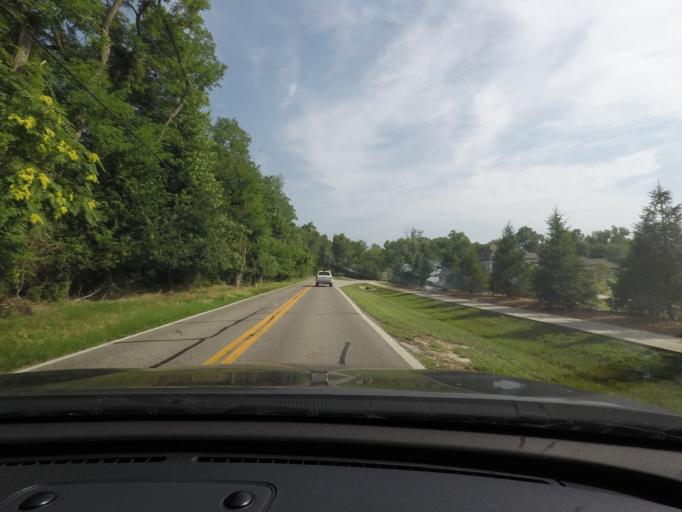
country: US
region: Missouri
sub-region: Saint Louis County
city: Town and Country
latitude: 38.6154
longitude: -90.4856
